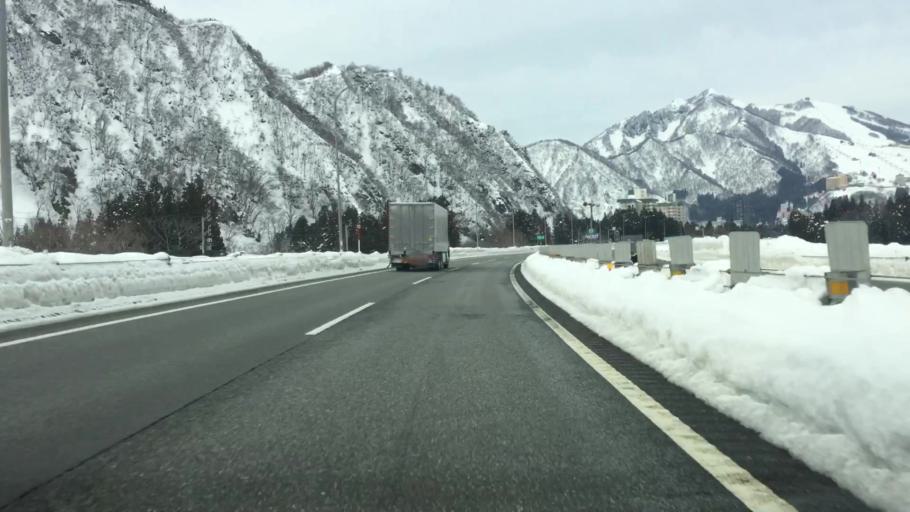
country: JP
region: Niigata
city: Shiozawa
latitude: 36.9107
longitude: 138.8402
